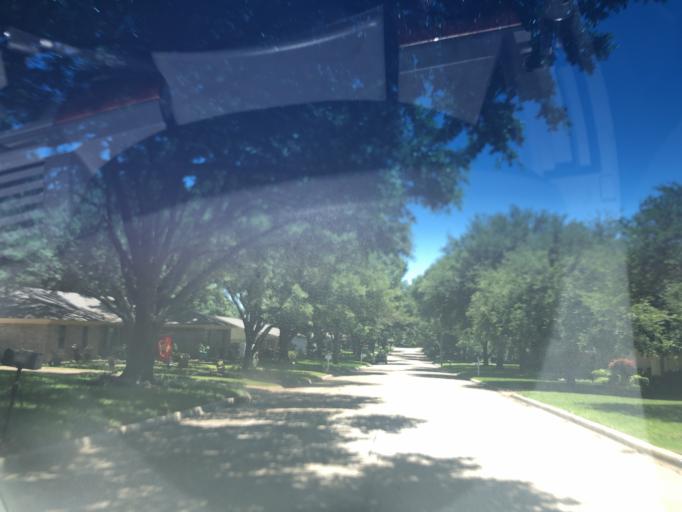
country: US
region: Texas
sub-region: Dallas County
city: Grand Prairie
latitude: 32.7751
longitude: -97.0391
